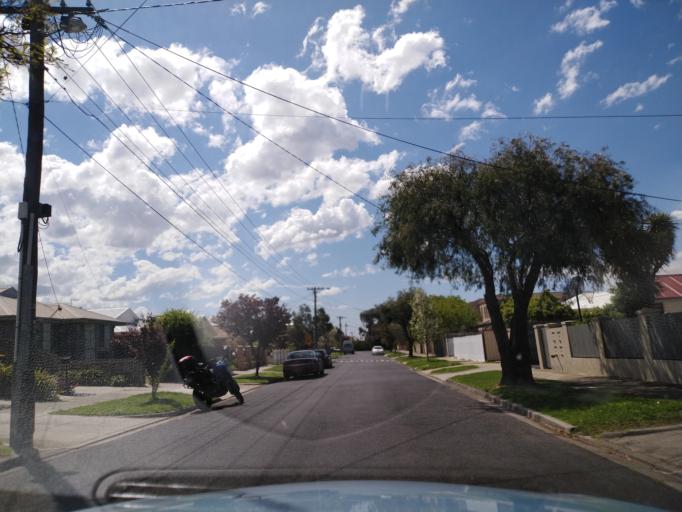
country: AU
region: Victoria
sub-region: Hobsons Bay
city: South Kingsville
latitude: -37.8301
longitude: 144.8728
